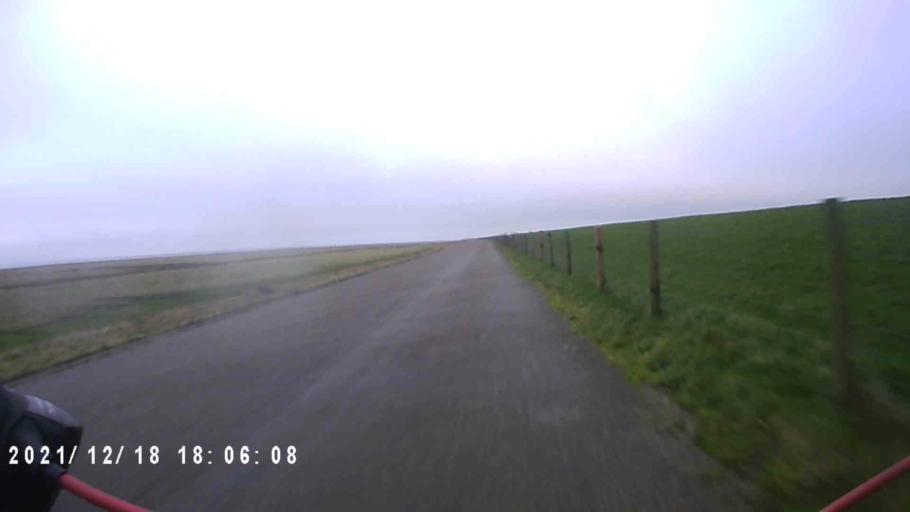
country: NL
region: Friesland
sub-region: Gemeente Dongeradeel
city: Holwerd
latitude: 53.3840
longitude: 5.9113
